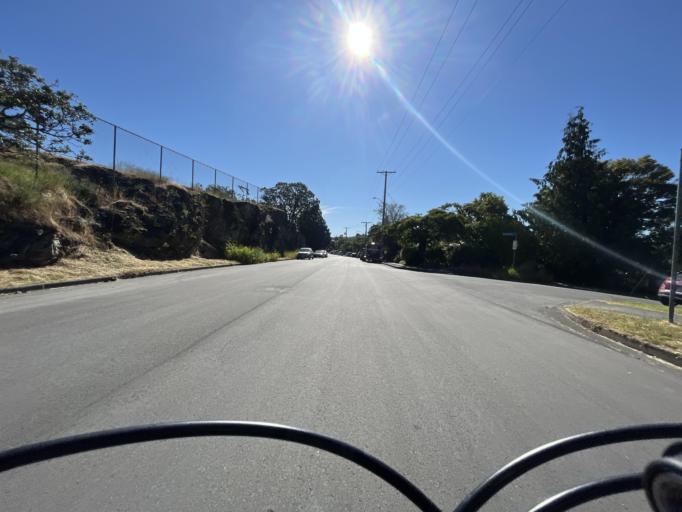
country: CA
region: British Columbia
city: Victoria
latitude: 48.4162
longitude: -123.3400
